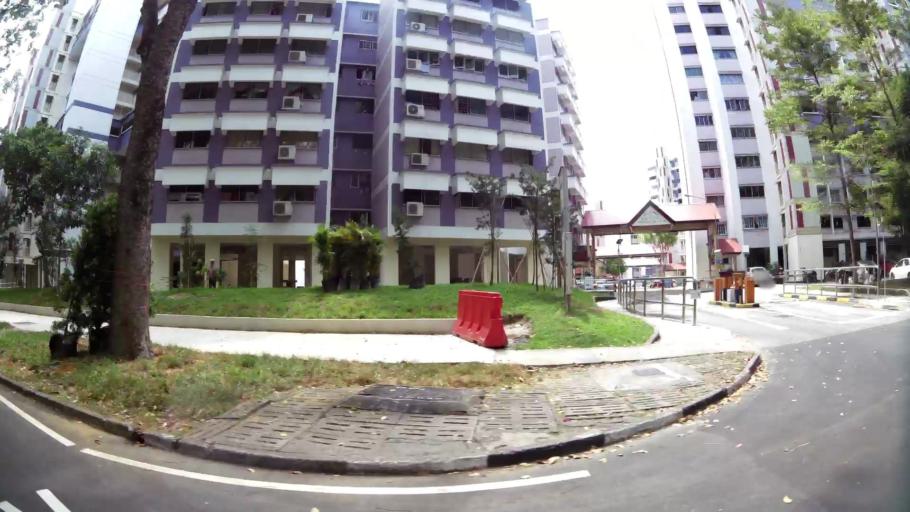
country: MY
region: Johor
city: Johor Bahru
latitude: 1.3527
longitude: 103.7179
